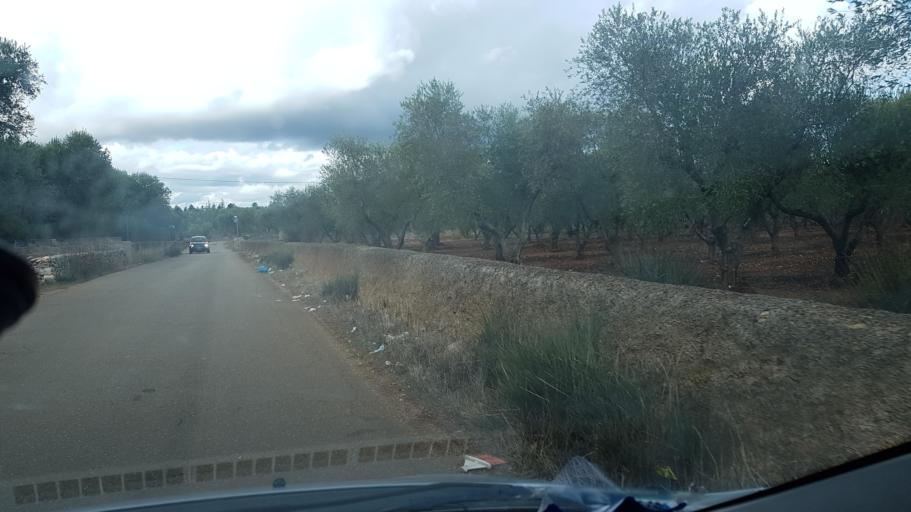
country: IT
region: Apulia
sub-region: Provincia di Brindisi
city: San Vito dei Normanni
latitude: 40.6520
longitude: 17.7273
